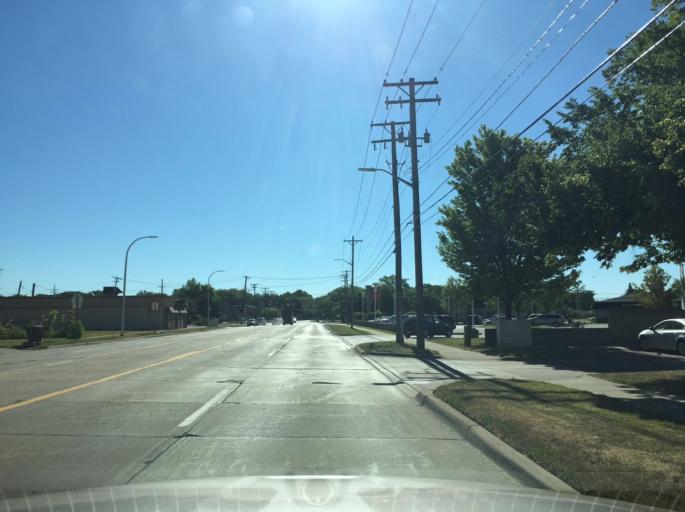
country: US
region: Michigan
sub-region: Macomb County
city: Saint Clair Shores
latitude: 42.5320
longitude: -82.8907
